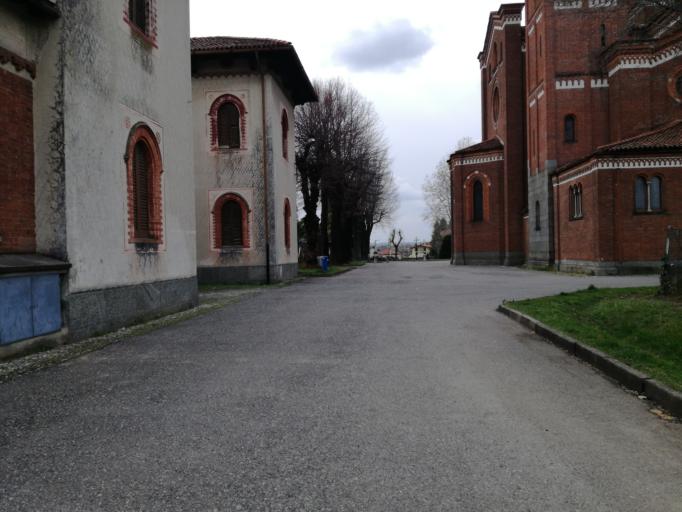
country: IT
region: Lombardy
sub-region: Provincia di Lecco
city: Verderio Superiore
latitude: 45.6667
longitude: 9.4402
